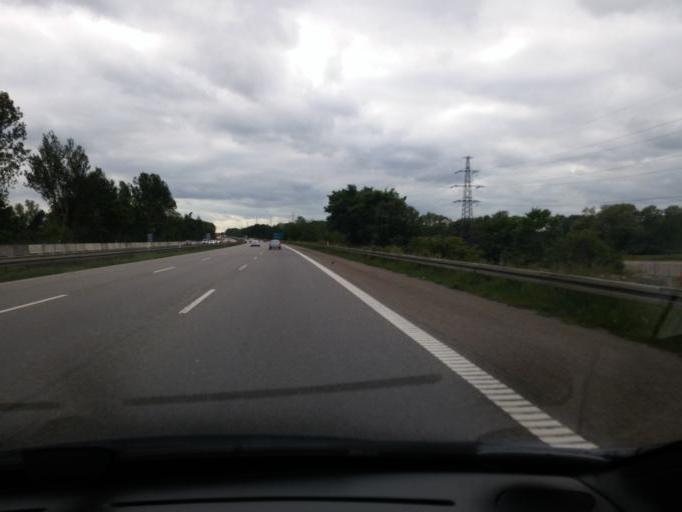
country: DK
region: Capital Region
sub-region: Vallensbaek Kommune
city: Vallensbaek
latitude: 55.6266
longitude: 12.3683
